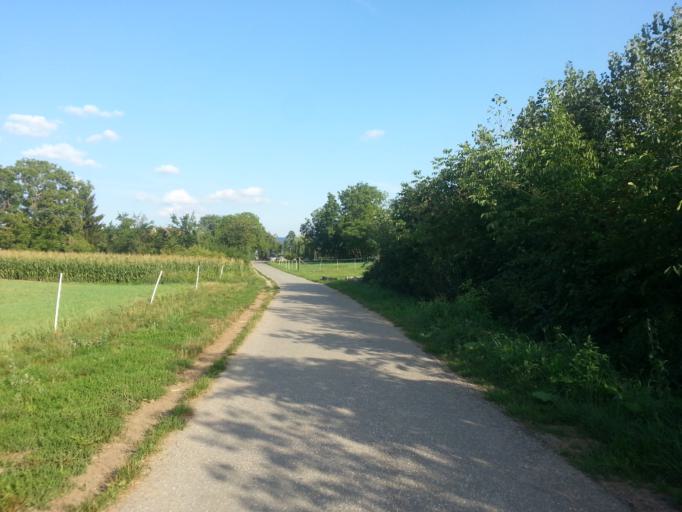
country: DE
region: Baden-Wuerttemberg
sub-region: Karlsruhe Region
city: Edingen-Neckarhausen
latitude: 49.4447
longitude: 8.6237
